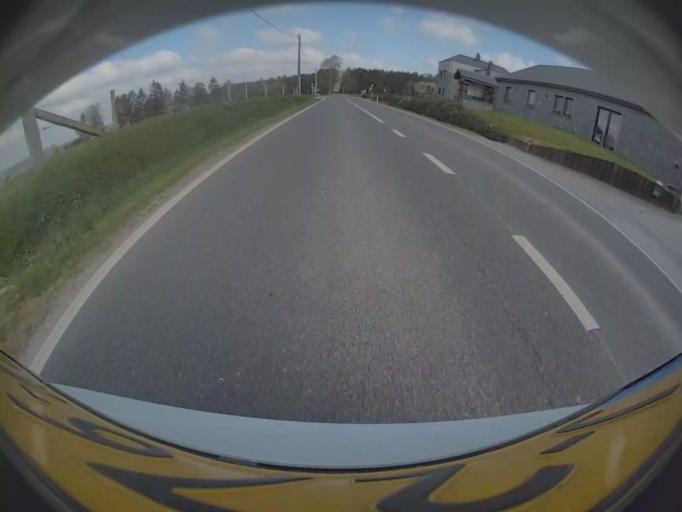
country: BE
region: Wallonia
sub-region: Province du Luxembourg
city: Tellin
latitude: 50.0946
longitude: 5.2322
